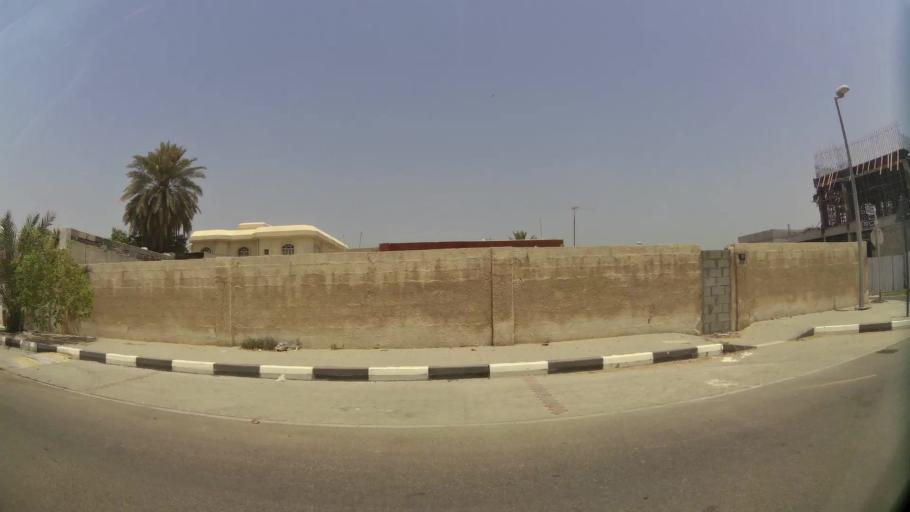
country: AE
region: Ash Shariqah
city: Sharjah
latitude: 25.3393
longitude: 55.3715
